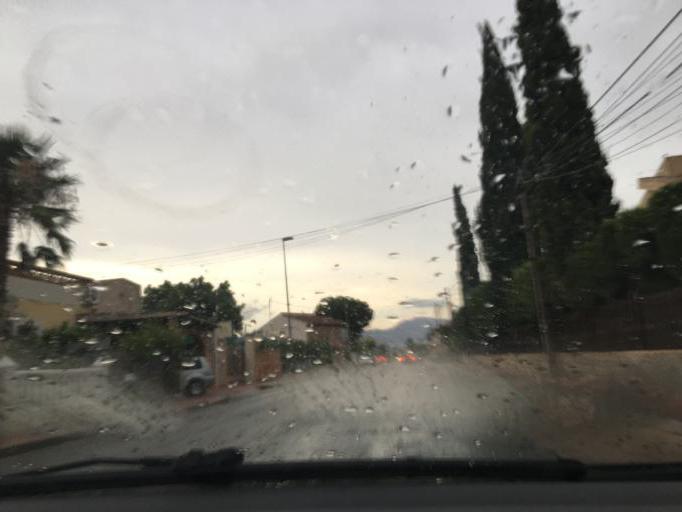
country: ES
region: Murcia
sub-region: Murcia
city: Santomera
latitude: 38.0269
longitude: -1.0466
